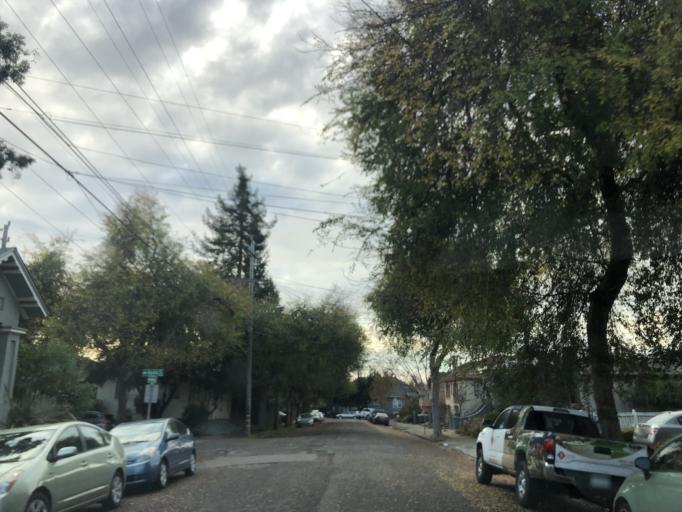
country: US
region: California
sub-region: Alameda County
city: Berkeley
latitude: 37.8461
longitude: -122.2569
